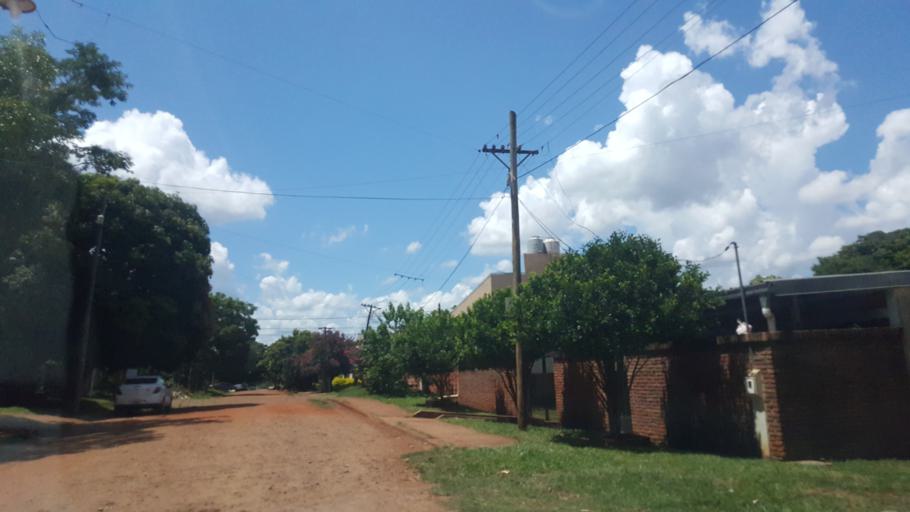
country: AR
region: Misiones
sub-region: Departamento de Capital
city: Posadas
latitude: -27.3712
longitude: -55.9187
